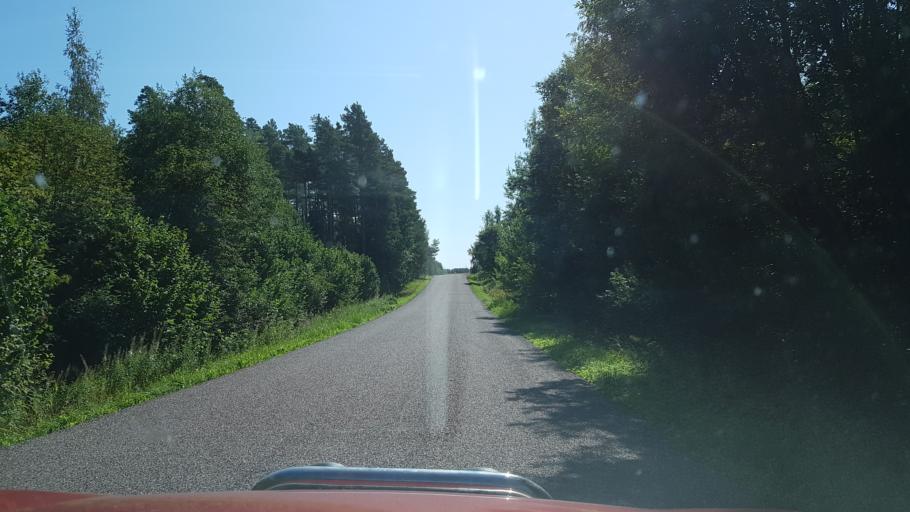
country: EE
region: Tartu
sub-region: Puhja vald
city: Puhja
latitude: 58.2531
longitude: 26.3300
